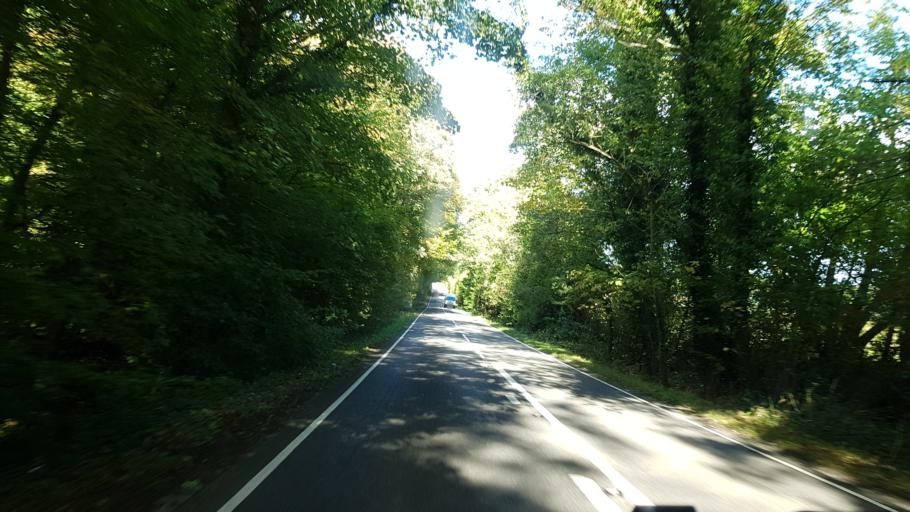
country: GB
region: England
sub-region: Surrey
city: Chiddingfold
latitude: 51.0850
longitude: -0.6487
